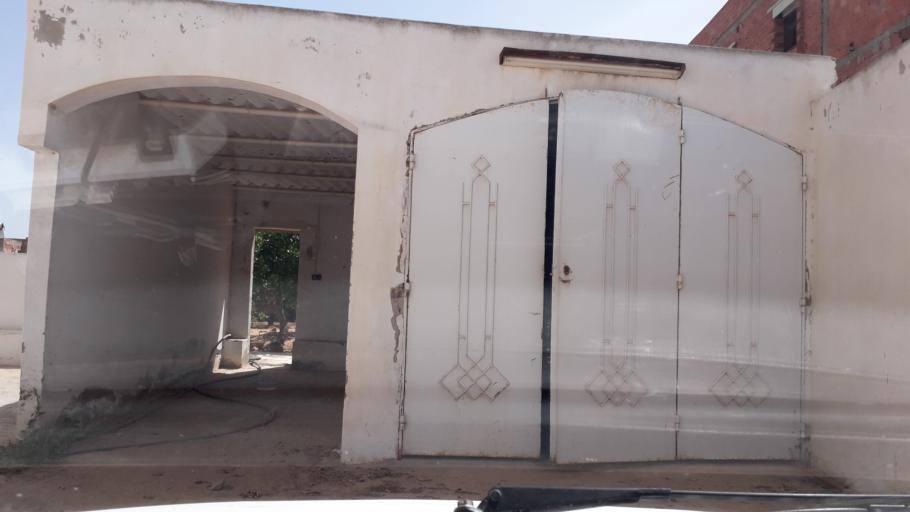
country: TN
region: Safaqis
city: Al Qarmadah
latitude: 34.7989
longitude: 10.7633
